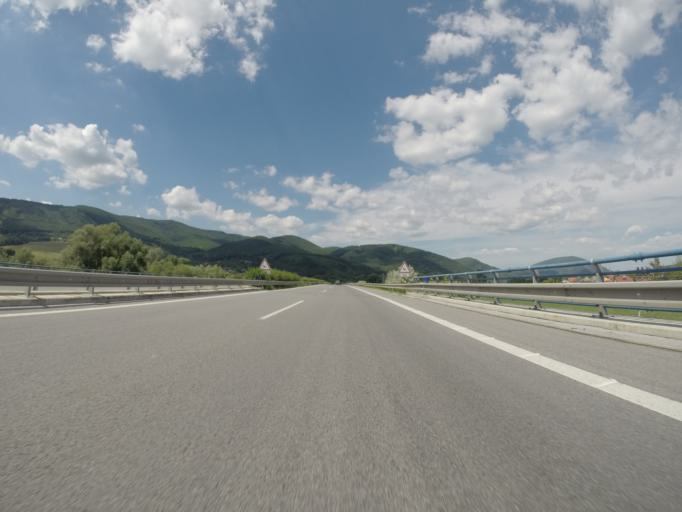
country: SK
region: Banskobystricky
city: Nova Bana
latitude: 48.3814
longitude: 18.6097
